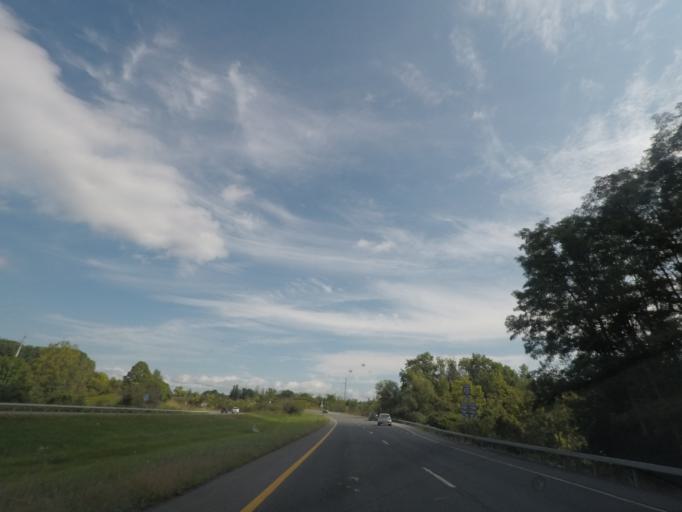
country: US
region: New York
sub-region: Albany County
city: Delmar
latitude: 42.6158
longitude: -73.7895
